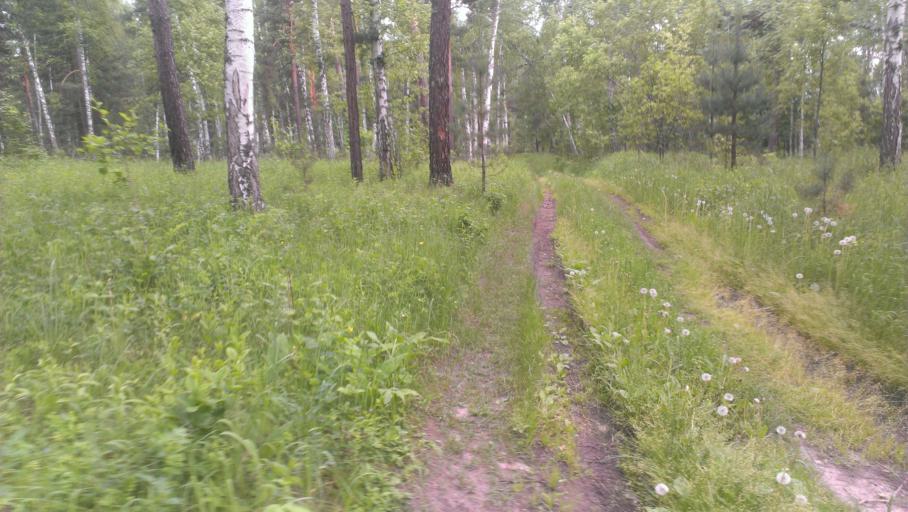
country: RU
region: Altai Krai
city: Sannikovo
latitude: 53.3391
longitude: 84.0496
